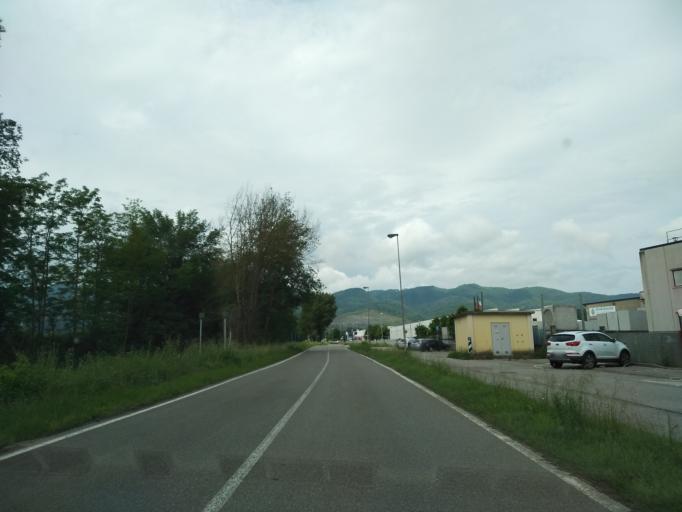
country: IT
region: Tuscany
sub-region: Province of Arezzo
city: San Cipriano-S.Barbara-Centinale
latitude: 43.5631
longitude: 11.4726
